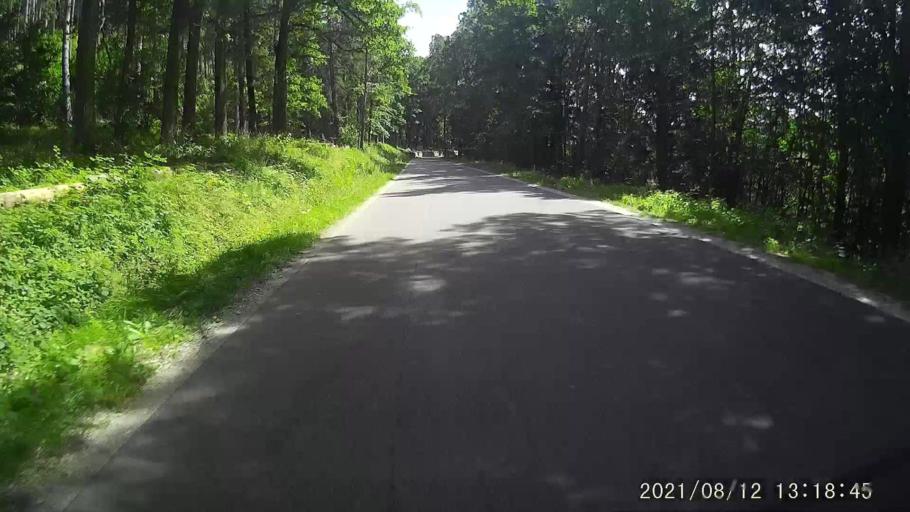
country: PL
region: Lower Silesian Voivodeship
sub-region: Powiat klodzki
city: Stronie Slaskie
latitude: 50.2736
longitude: 16.8883
